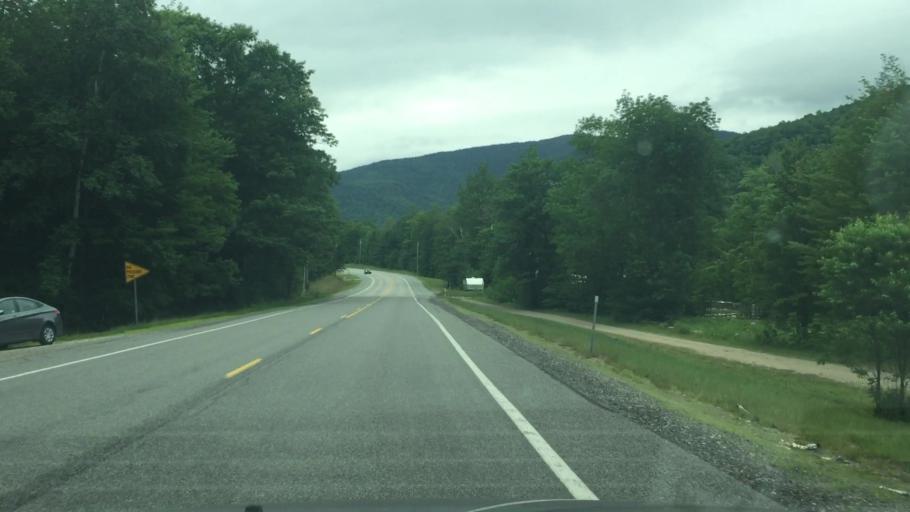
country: US
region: New Hampshire
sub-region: Carroll County
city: North Conway
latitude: 44.1037
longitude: -71.3528
